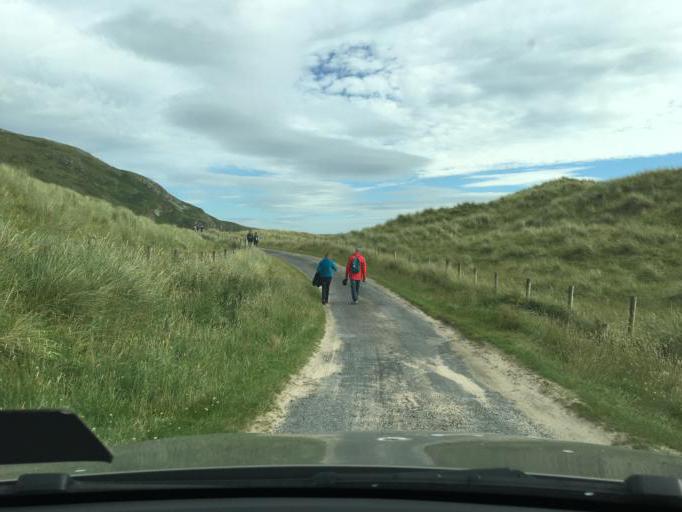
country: IE
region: Ulster
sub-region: County Donegal
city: Carndonagh
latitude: 55.3226
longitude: -7.3285
